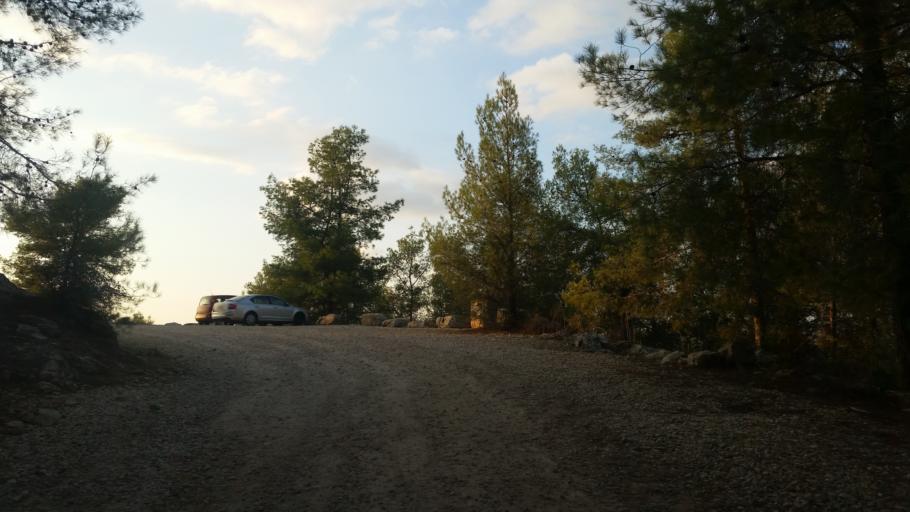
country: IL
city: Hashmonaim
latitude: 31.9236
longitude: 35.0115
